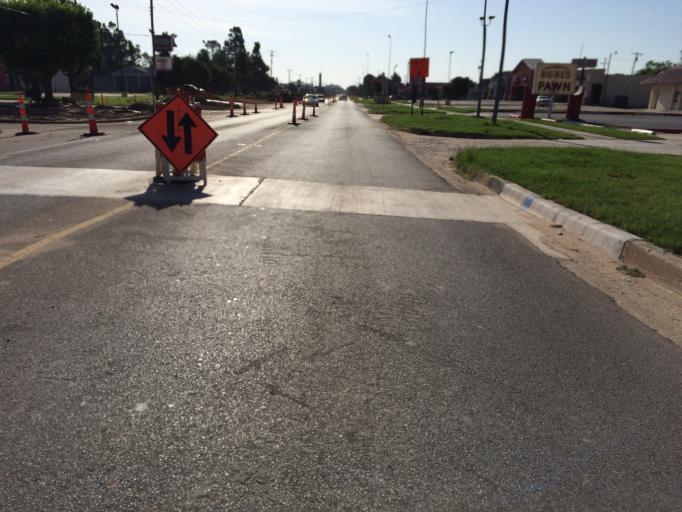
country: US
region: Oklahoma
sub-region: Cleveland County
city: Norman
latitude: 35.2039
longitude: -97.4740
